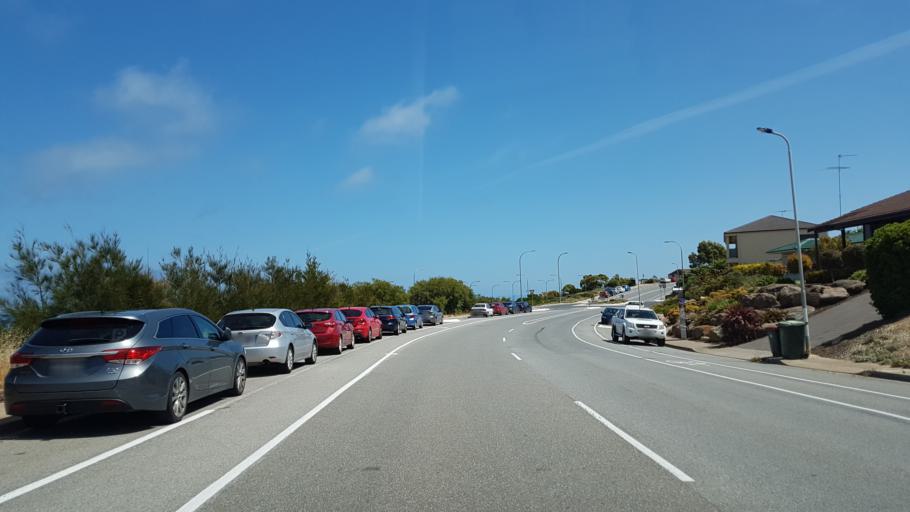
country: AU
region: South Australia
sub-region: Marion
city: Marino
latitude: -35.0692
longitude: 138.5067
